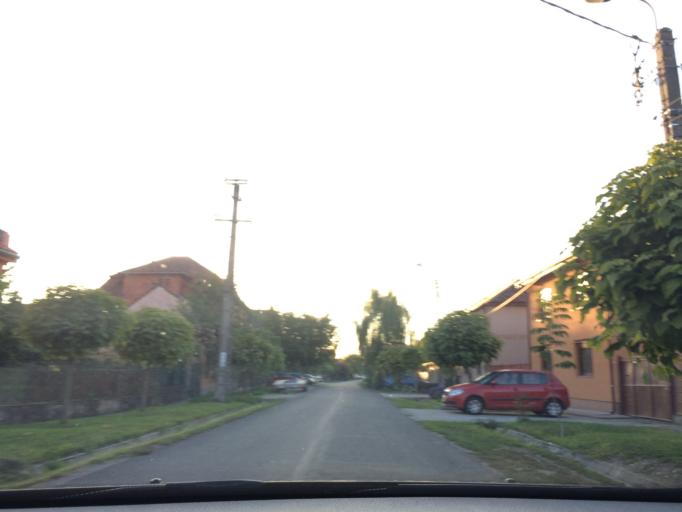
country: RO
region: Timis
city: Timisoara
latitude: 45.7635
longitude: 21.2015
